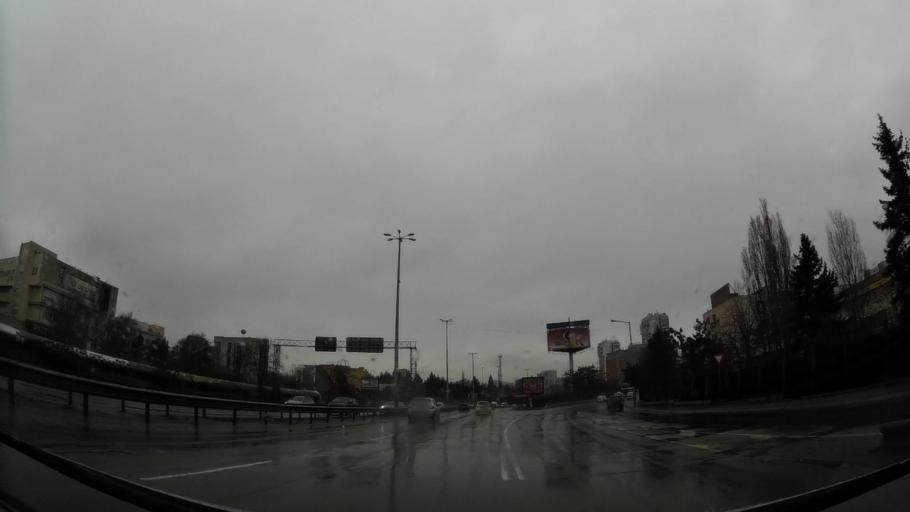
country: BG
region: Sofia-Capital
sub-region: Stolichna Obshtina
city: Sofia
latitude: 42.6585
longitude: 23.3868
